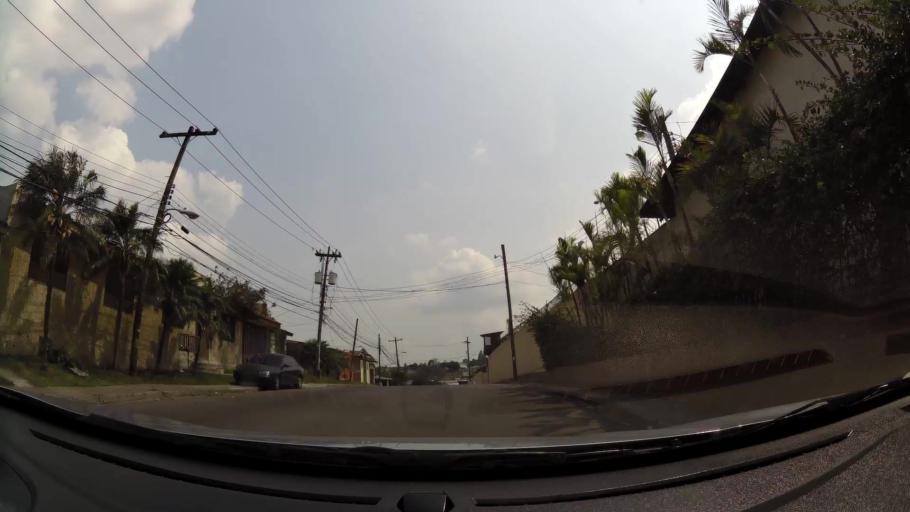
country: HN
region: Francisco Morazan
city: El Lolo
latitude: 14.1232
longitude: -87.2232
